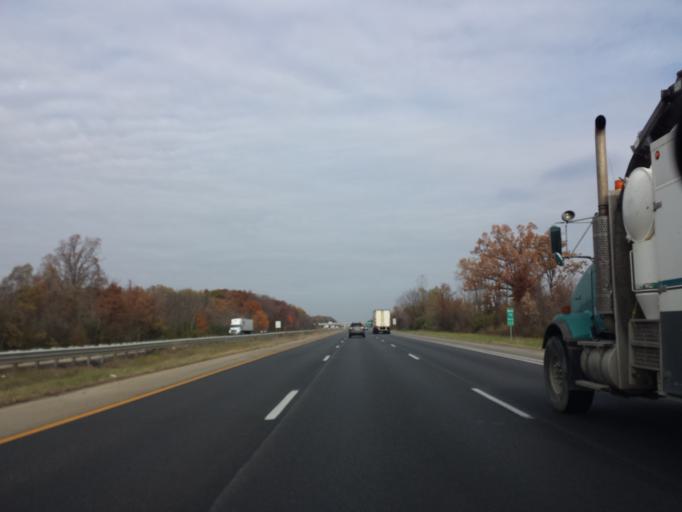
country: US
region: Michigan
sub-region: Genesee County
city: Beecher
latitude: 43.0692
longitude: -83.7625
